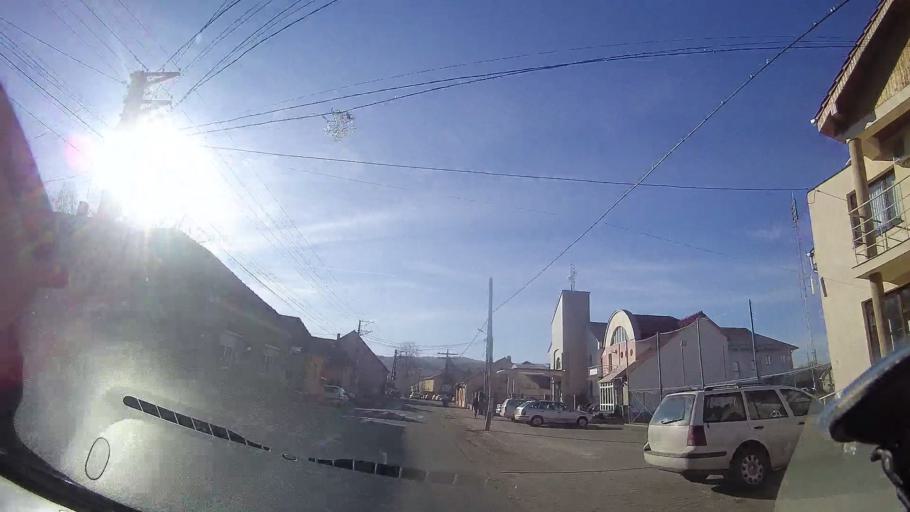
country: RO
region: Bihor
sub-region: Comuna Vadu Crisului
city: Vadu Crisului
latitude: 46.9864
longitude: 22.5161
